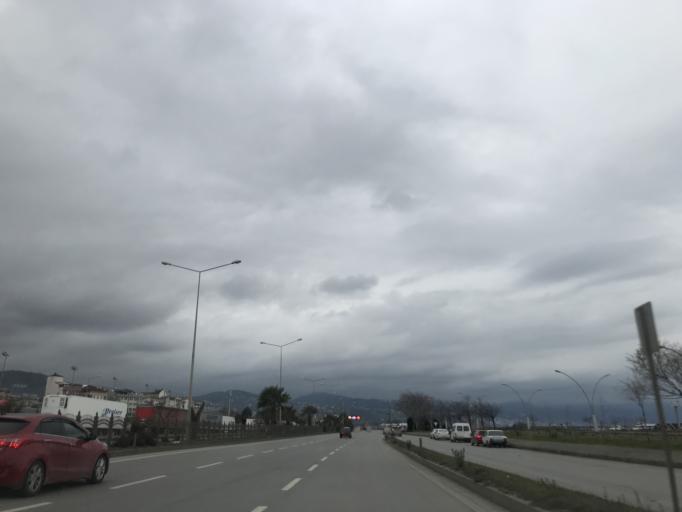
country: TR
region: Trabzon
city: Trabzon
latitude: 41.0096
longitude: 39.7102
